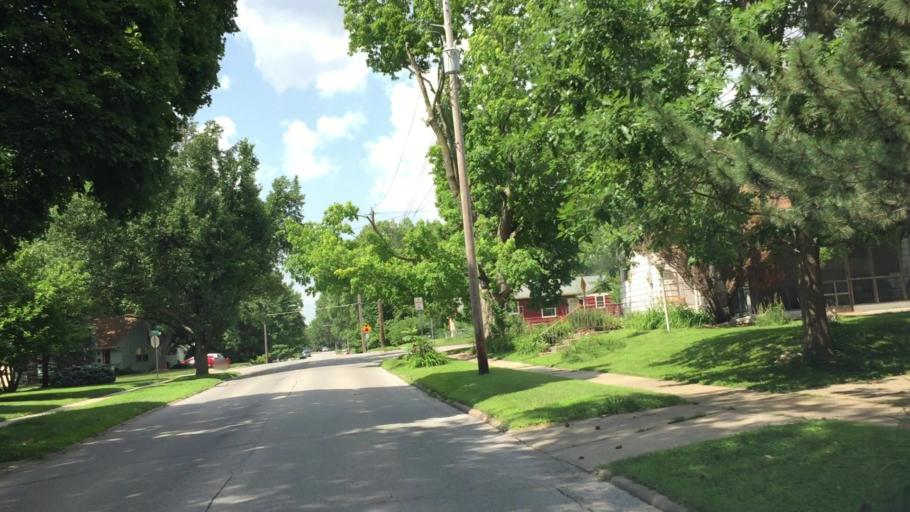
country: US
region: Iowa
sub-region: Johnson County
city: Iowa City
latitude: 41.6594
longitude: -91.5117
